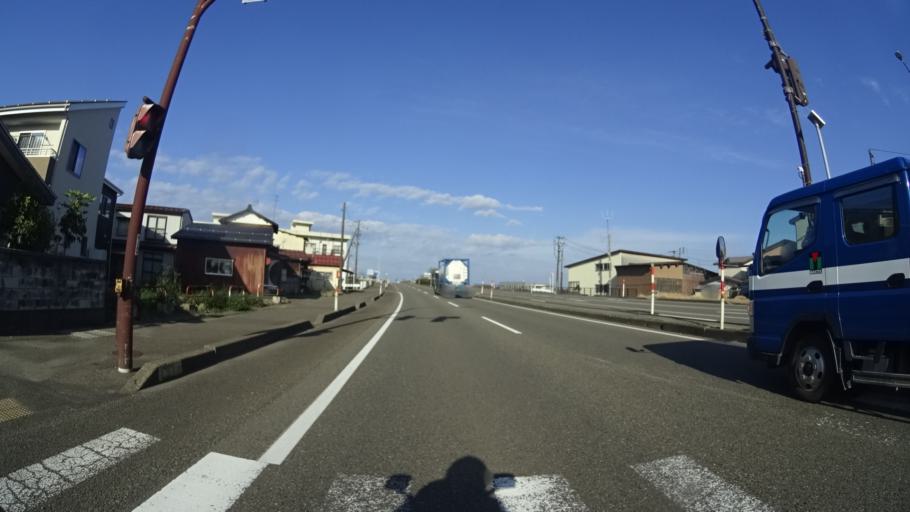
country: JP
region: Niigata
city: Joetsu
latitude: 37.1782
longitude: 138.2684
